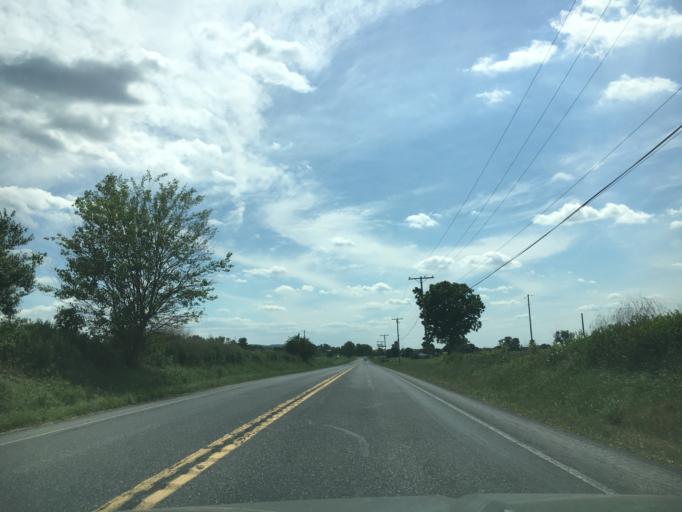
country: US
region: Pennsylvania
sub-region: Berks County
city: Fleetwood
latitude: 40.4739
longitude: -75.7912
